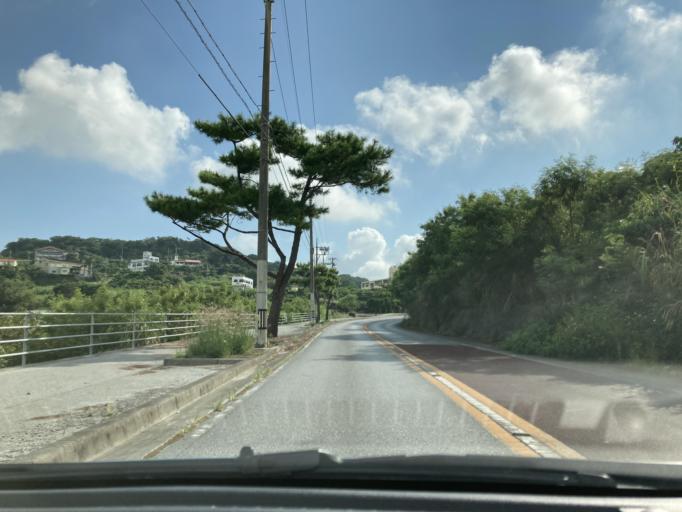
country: JP
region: Okinawa
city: Tomigusuku
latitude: 26.1479
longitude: 127.7578
